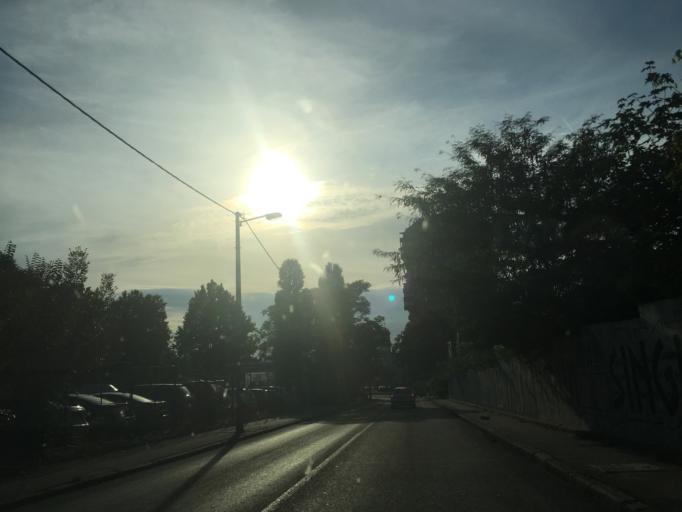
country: RS
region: Central Serbia
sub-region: Belgrade
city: Palilula
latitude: 44.8147
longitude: 20.4933
